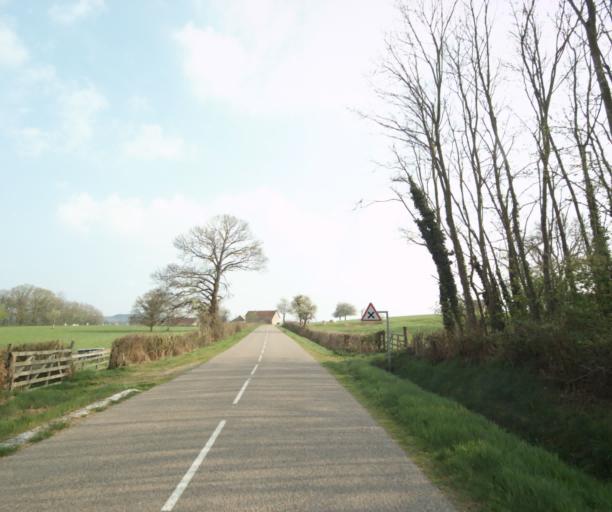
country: FR
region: Bourgogne
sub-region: Departement de Saone-et-Loire
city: Charolles
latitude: 46.4620
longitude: 4.4396
